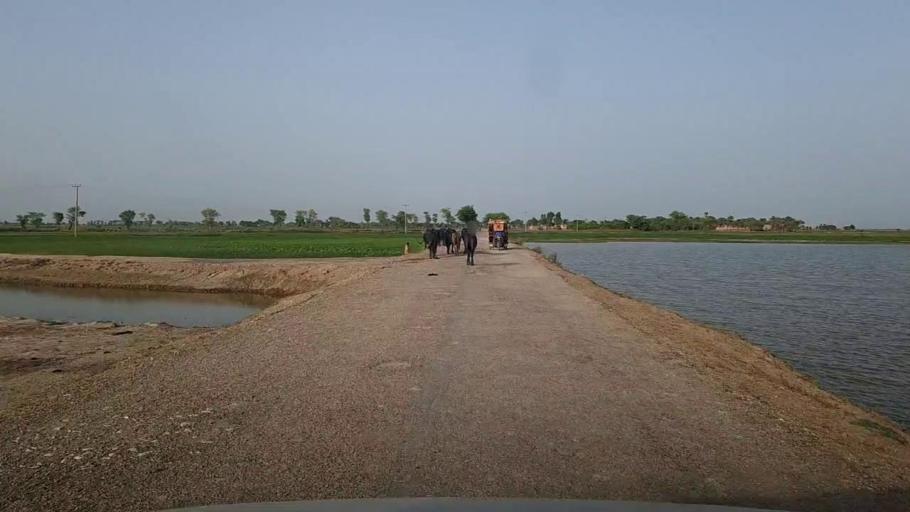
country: PK
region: Sindh
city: Khairpur Nathan Shah
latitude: 27.1576
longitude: 67.7489
